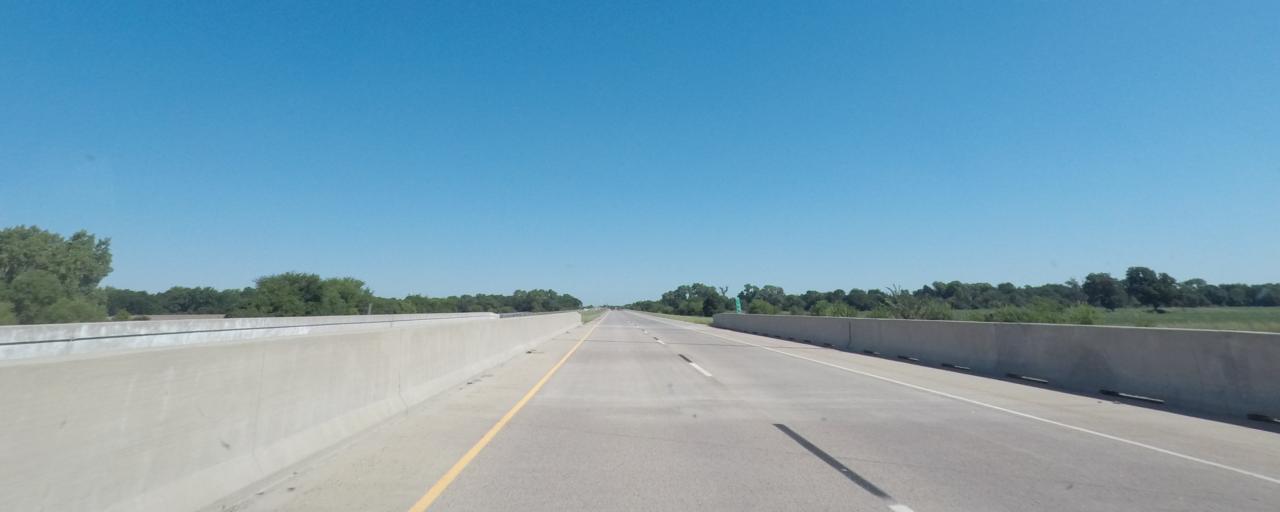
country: US
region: Oklahoma
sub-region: Noble County
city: Perry
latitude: 36.4700
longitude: -97.3269
